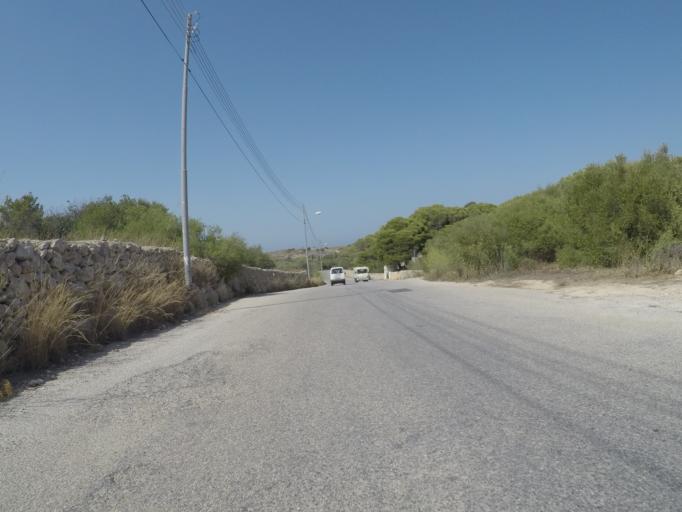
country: MT
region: L-Imgarr
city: Imgarr
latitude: 35.9319
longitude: 14.3760
